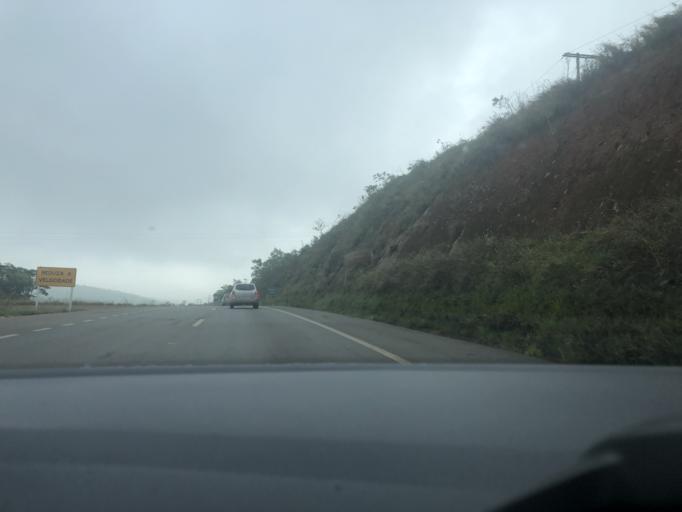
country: BR
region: Minas Gerais
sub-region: Congonhas
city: Congonhas
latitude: -20.5916
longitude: -43.9418
